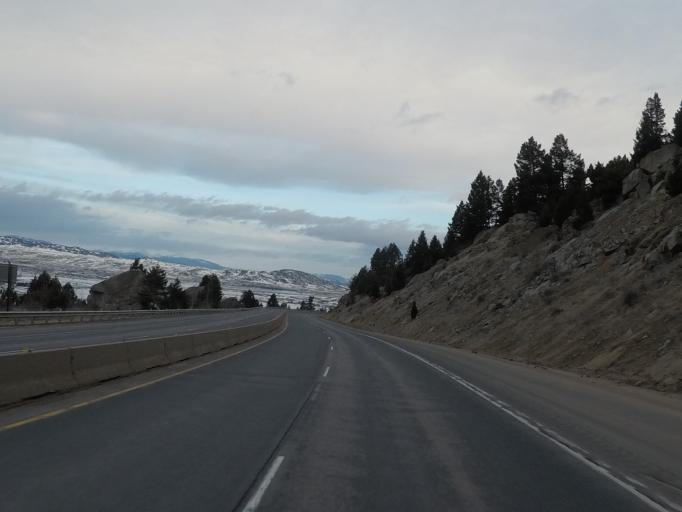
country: US
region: Montana
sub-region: Silver Bow County
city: Butte
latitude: 45.9289
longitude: -112.4459
